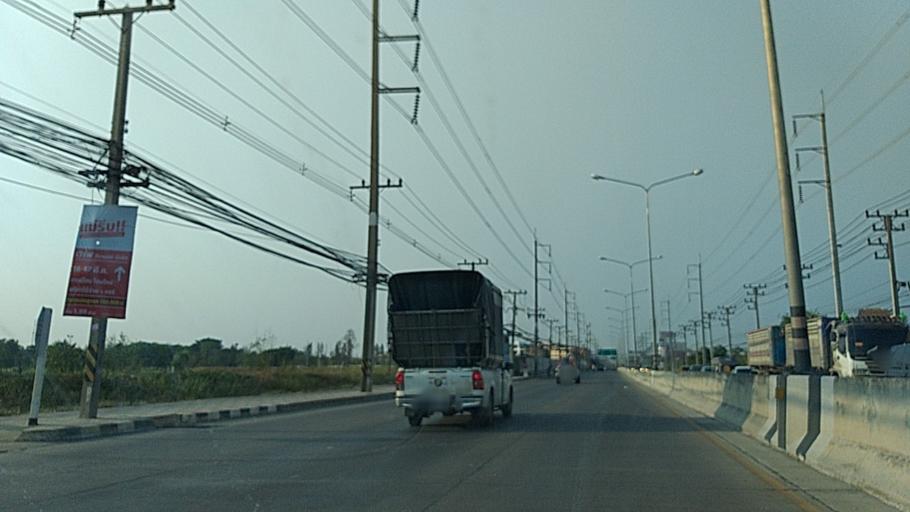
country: TH
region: Phra Nakhon Si Ayutthaya
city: Ban Bang Kadi Pathum Thani
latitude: 13.9774
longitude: 100.5506
